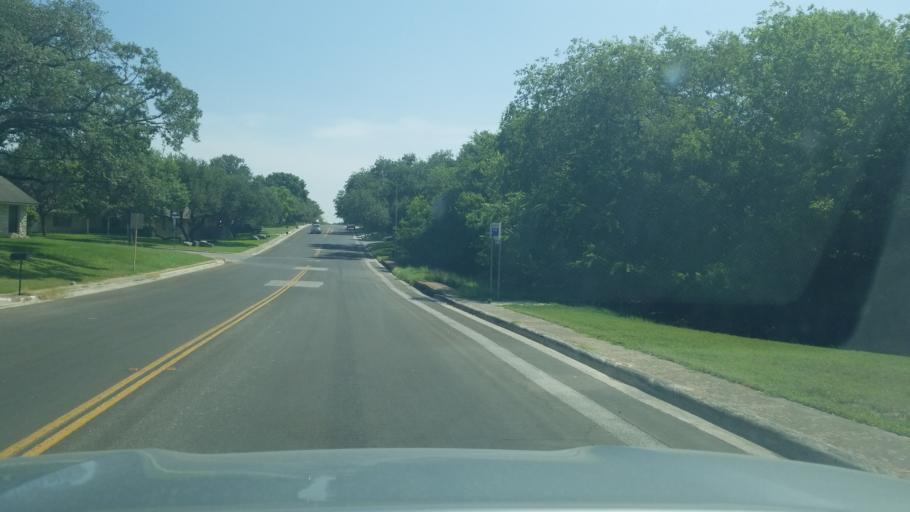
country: US
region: Texas
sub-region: Bexar County
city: Hollywood Park
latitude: 29.5844
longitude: -98.4636
